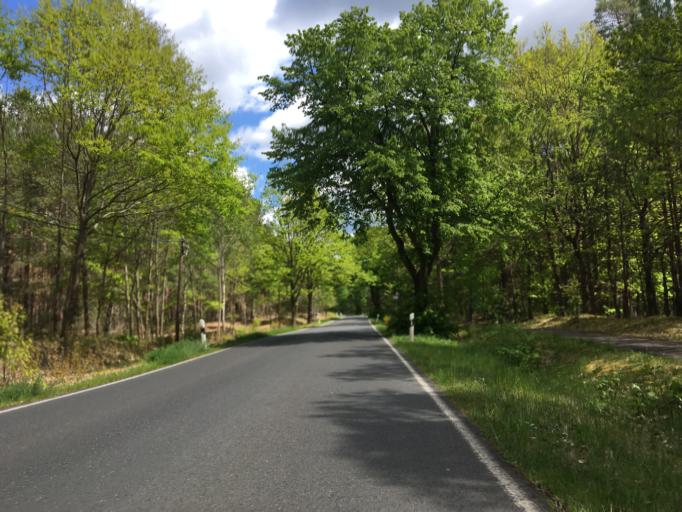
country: DE
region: Brandenburg
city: Liebenwalde
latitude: 52.8879
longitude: 13.4854
